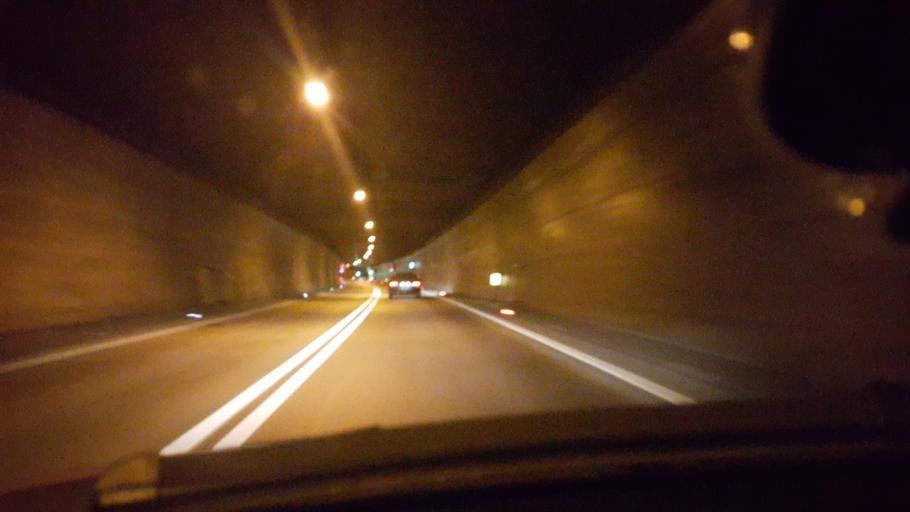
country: AT
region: Styria
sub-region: Graz Stadt
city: Wetzelsdorf
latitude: 47.0529
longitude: 15.3995
